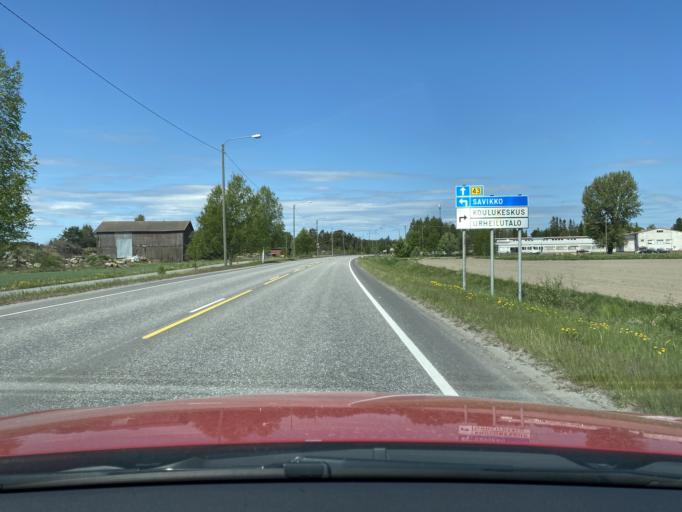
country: FI
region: Satakunta
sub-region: Rauma
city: Eura
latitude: 61.1224
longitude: 22.1332
